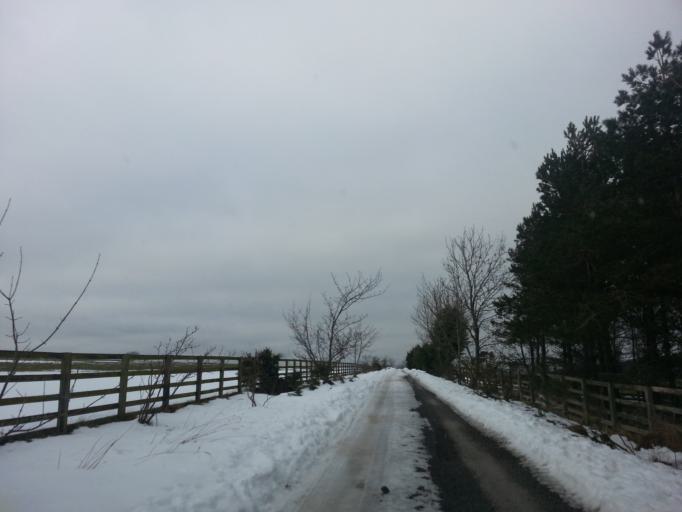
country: GB
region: England
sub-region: County Durham
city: Tow Law
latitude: 54.7698
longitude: -1.7929
